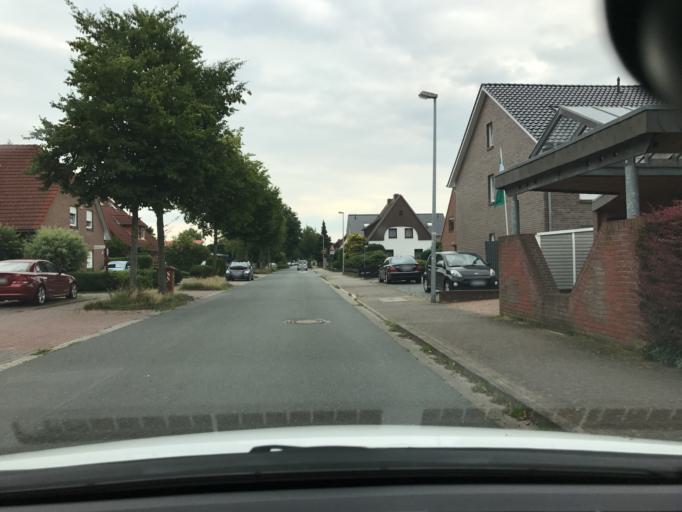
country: DE
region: Lower Saxony
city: Syke
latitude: 52.9874
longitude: 8.8634
